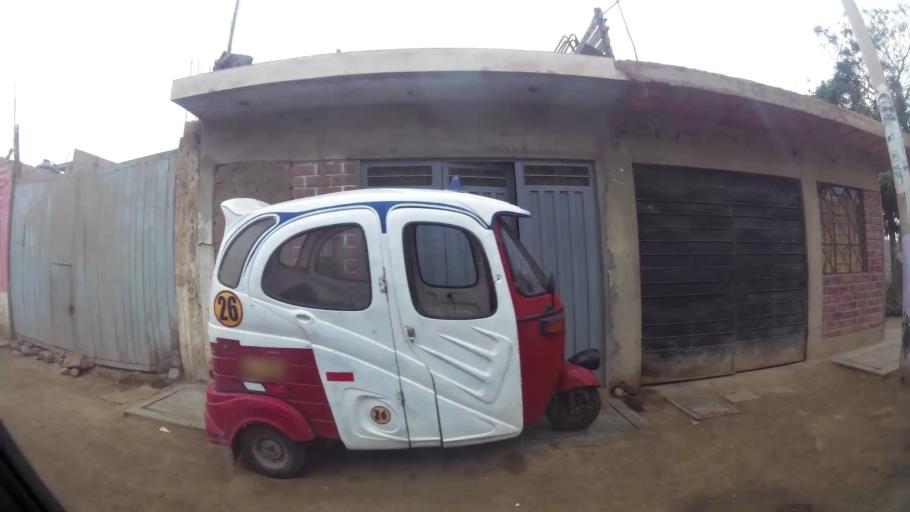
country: PE
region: Lima
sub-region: Provincia de Huaral
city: Huaral
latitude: -11.5010
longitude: -77.2207
